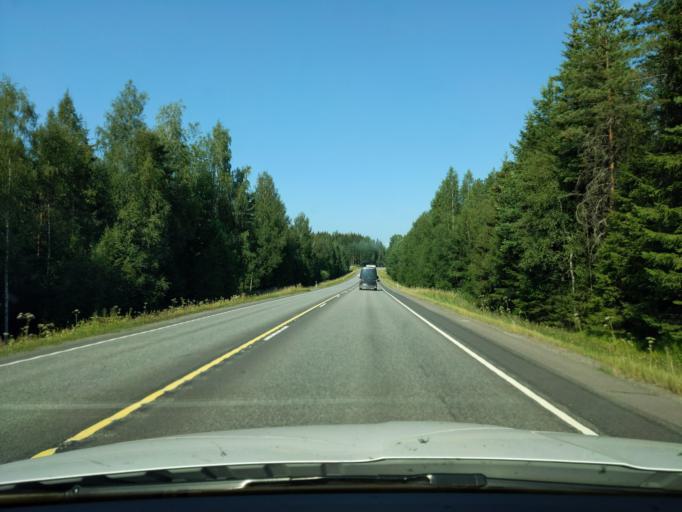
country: FI
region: Paijanne Tavastia
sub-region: Lahti
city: Hollola
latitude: 60.9595
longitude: 25.4443
